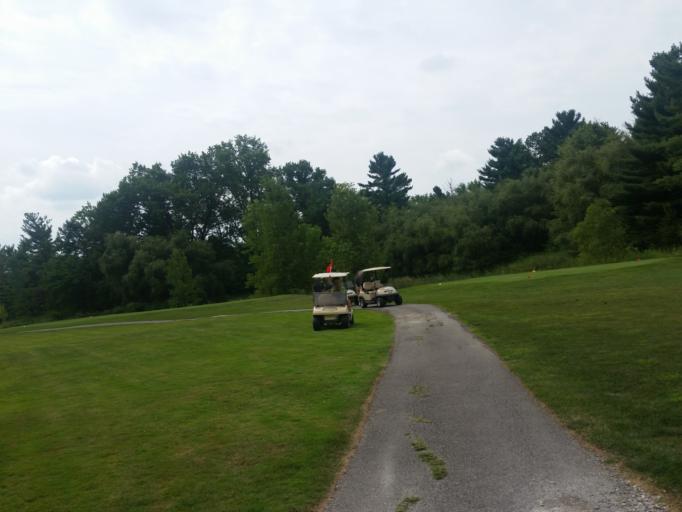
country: US
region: Ohio
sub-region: Cuyahoga County
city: Olmsted Falls
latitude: 41.3957
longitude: -81.9079
